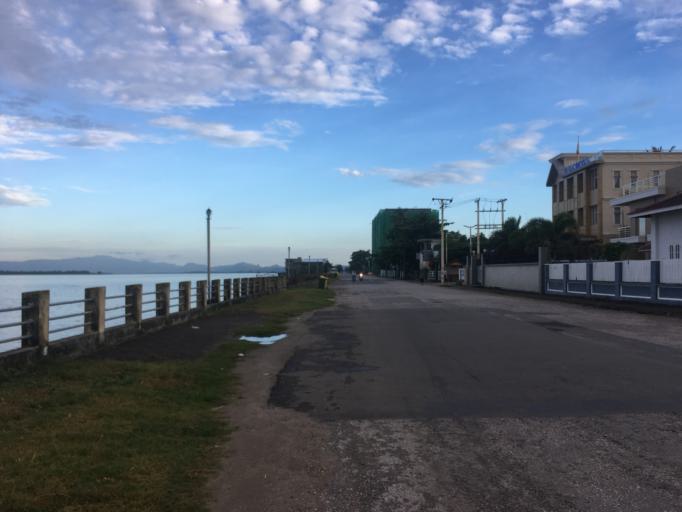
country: MM
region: Mon
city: Mawlamyine
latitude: 16.4685
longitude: 97.6216
